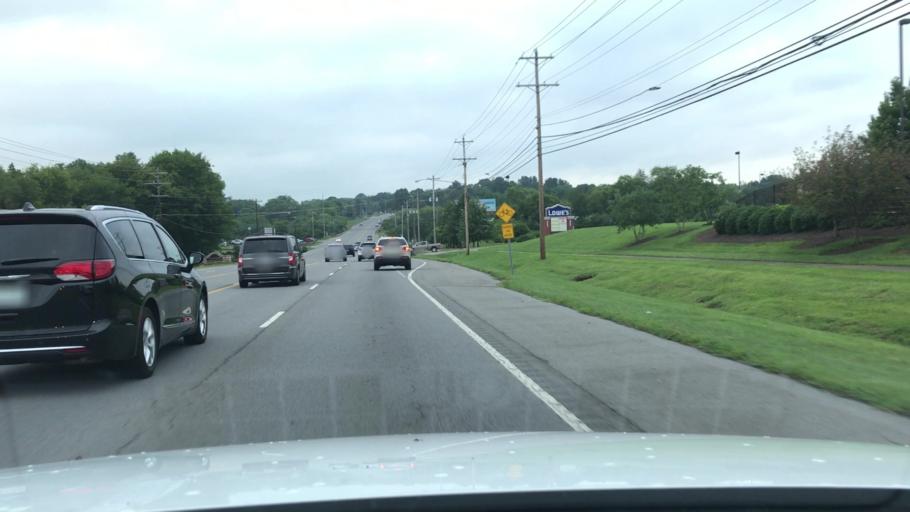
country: US
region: Tennessee
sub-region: Sumner County
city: Gallatin
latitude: 36.3667
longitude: -86.4890
